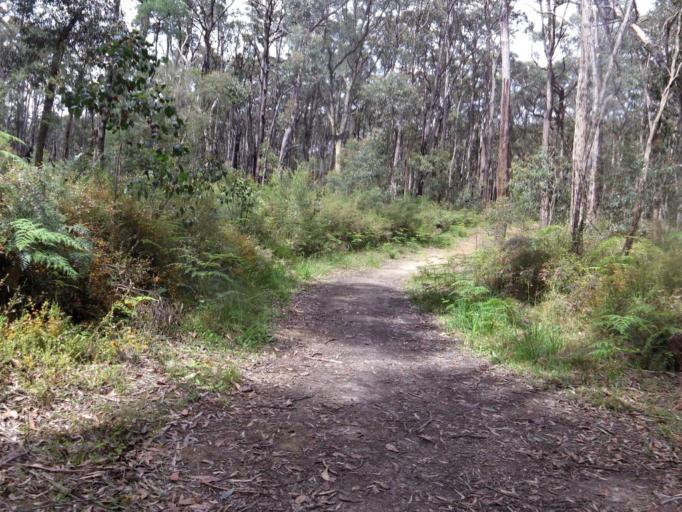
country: AU
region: Victoria
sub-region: Cardinia
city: Cockatoo
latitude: -37.9284
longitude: 145.4811
